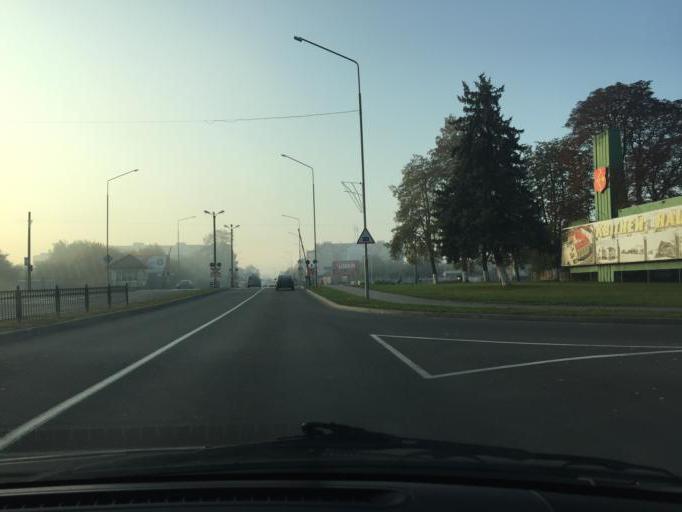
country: BY
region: Brest
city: Pinsk
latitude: 52.1233
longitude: 26.1000
